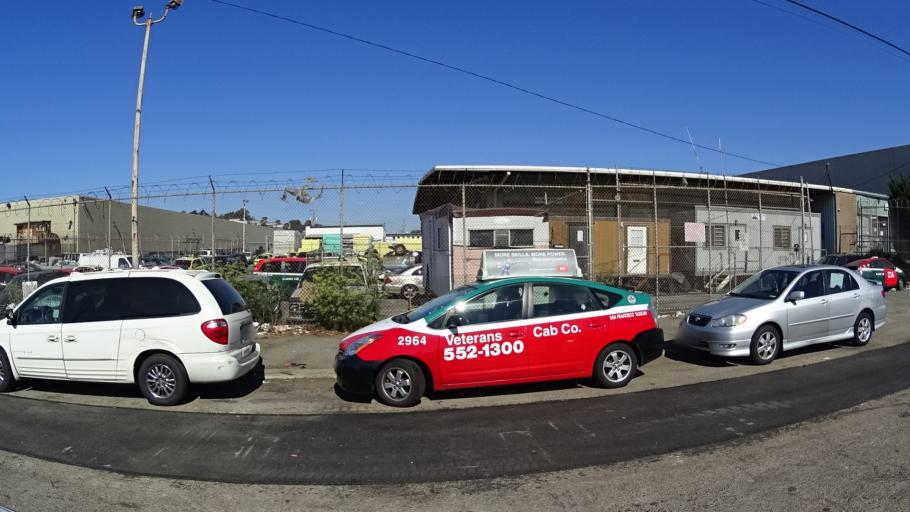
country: US
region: California
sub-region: San Francisco County
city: San Francisco
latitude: 37.7430
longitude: -122.4018
